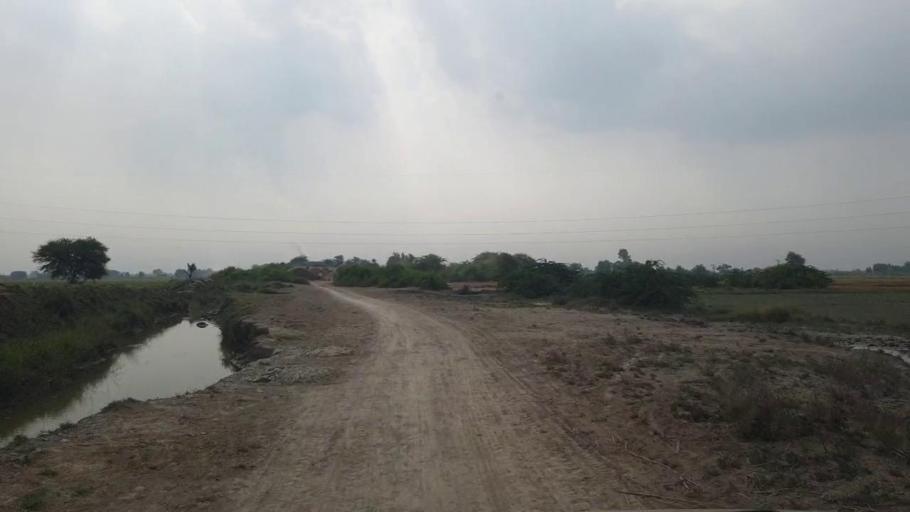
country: PK
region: Sindh
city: Talhar
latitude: 24.8819
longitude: 68.7882
